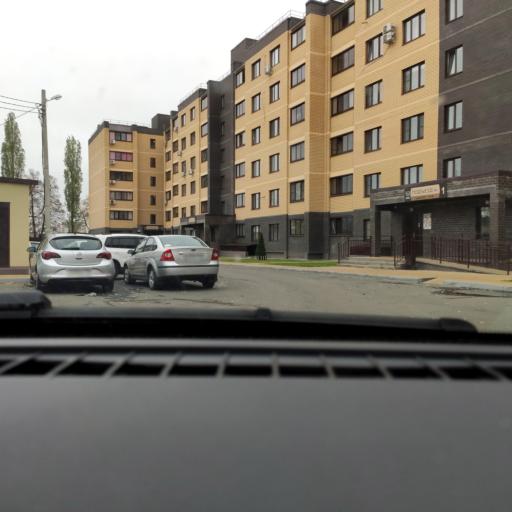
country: RU
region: Voronezj
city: Voronezh
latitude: 51.6667
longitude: 39.2794
